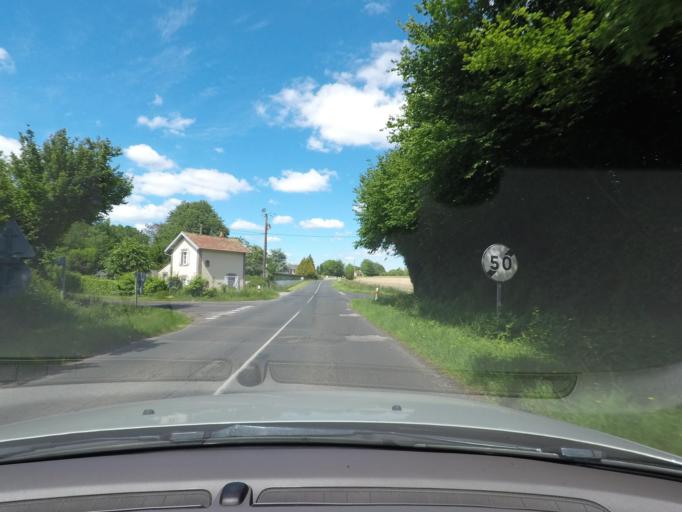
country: FR
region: Lower Normandy
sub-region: Departement de l'Orne
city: Mortagne-au-Perche
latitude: 48.5414
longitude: 0.5636
